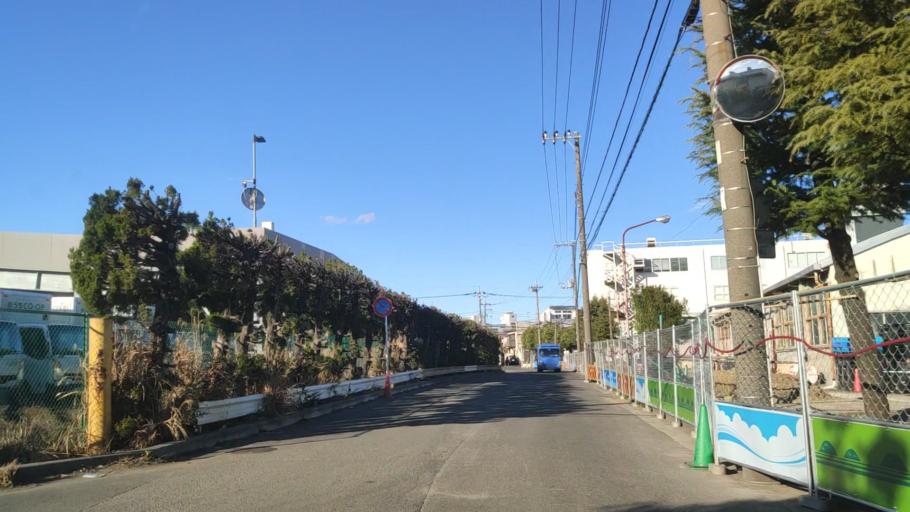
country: JP
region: Tokyo
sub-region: Machida-shi
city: Machida
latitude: 35.5172
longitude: 139.5485
